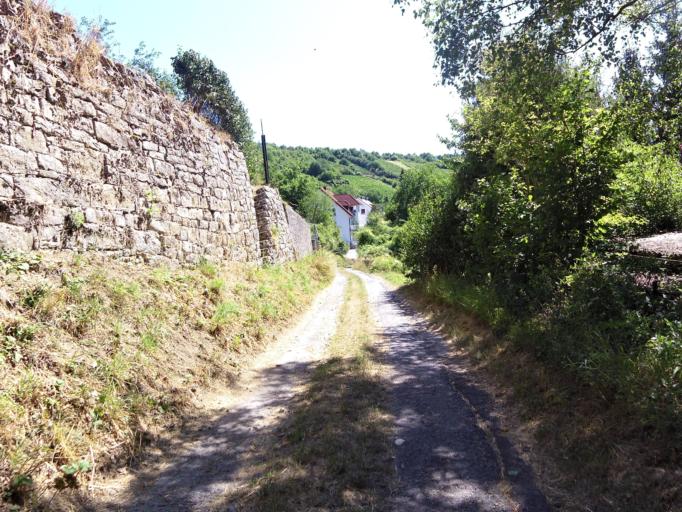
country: DE
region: Bavaria
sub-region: Regierungsbezirk Unterfranken
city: Randersacker
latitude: 49.7639
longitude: 9.9906
